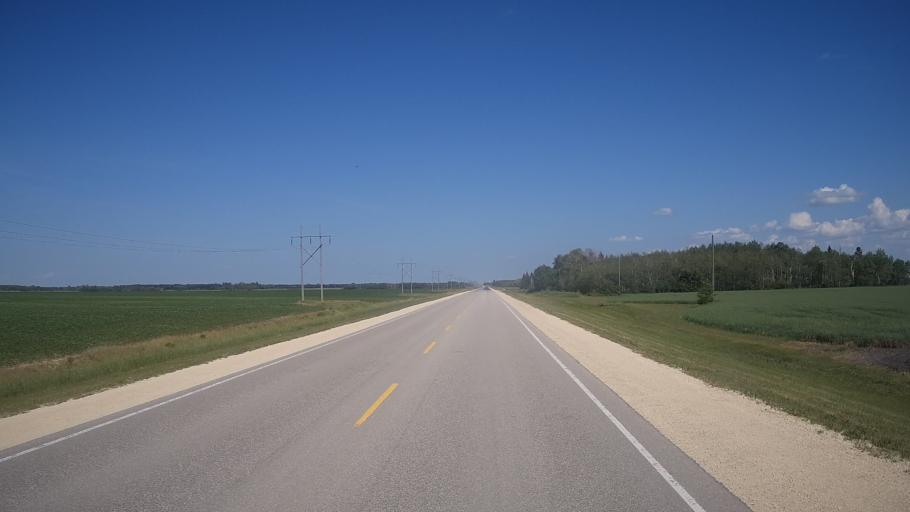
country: CA
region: Manitoba
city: Stonewall
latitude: 50.1227
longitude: -97.3881
